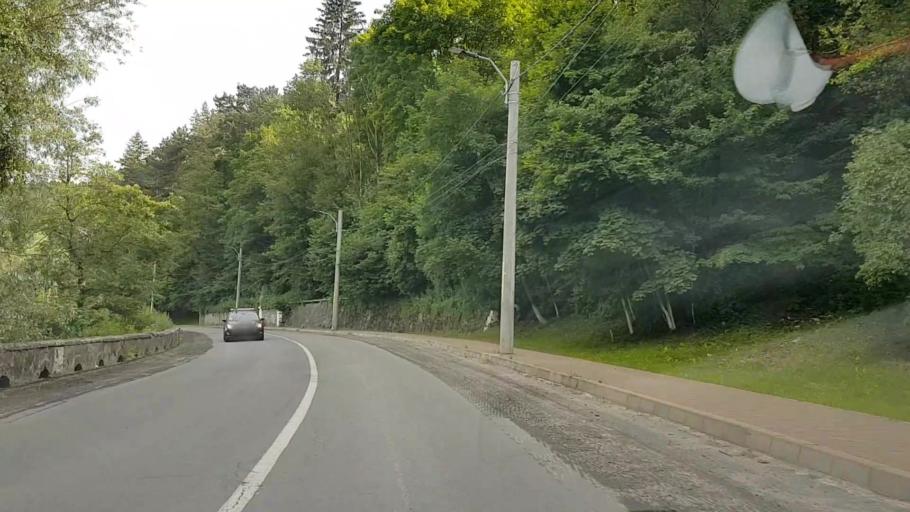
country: RO
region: Neamt
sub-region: Comuna Bicaz
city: Dodeni
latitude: 46.9178
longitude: 26.0842
